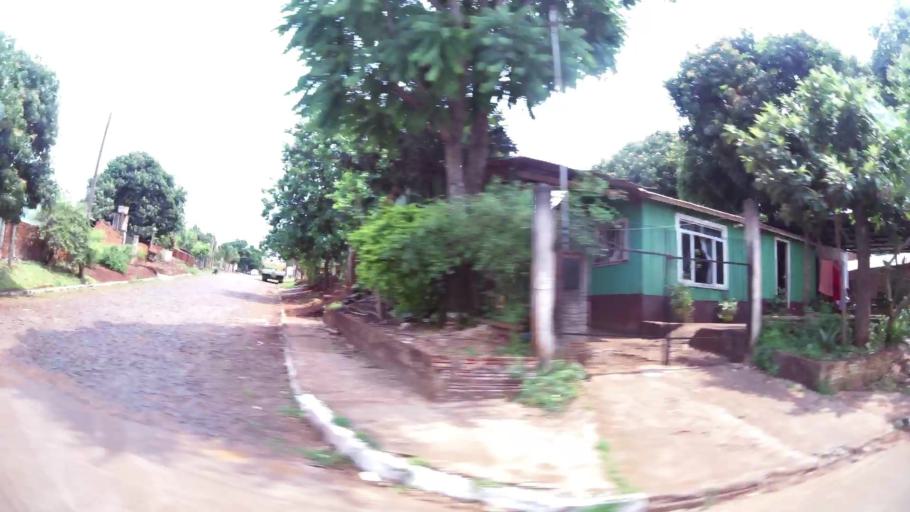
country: BR
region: Parana
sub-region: Foz Do Iguacu
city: Foz do Iguacu
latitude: -25.5684
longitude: -54.6073
